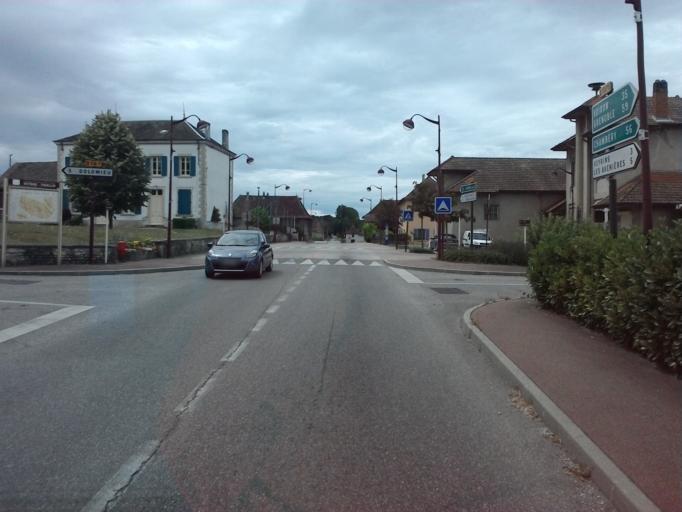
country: FR
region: Rhone-Alpes
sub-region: Departement de l'Isere
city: Thuellin
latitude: 45.6396
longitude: 5.5087
